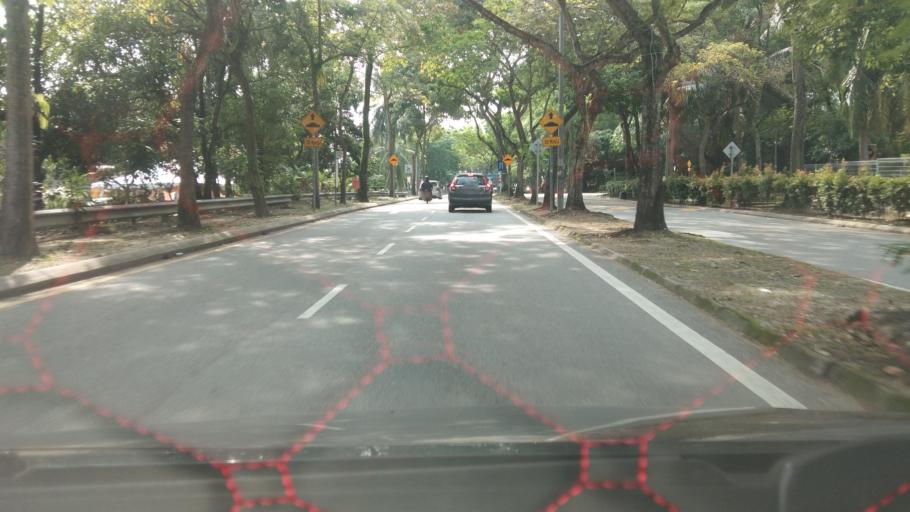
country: MY
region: Selangor
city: Kampong Baharu Balakong
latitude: 3.0736
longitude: 101.7139
